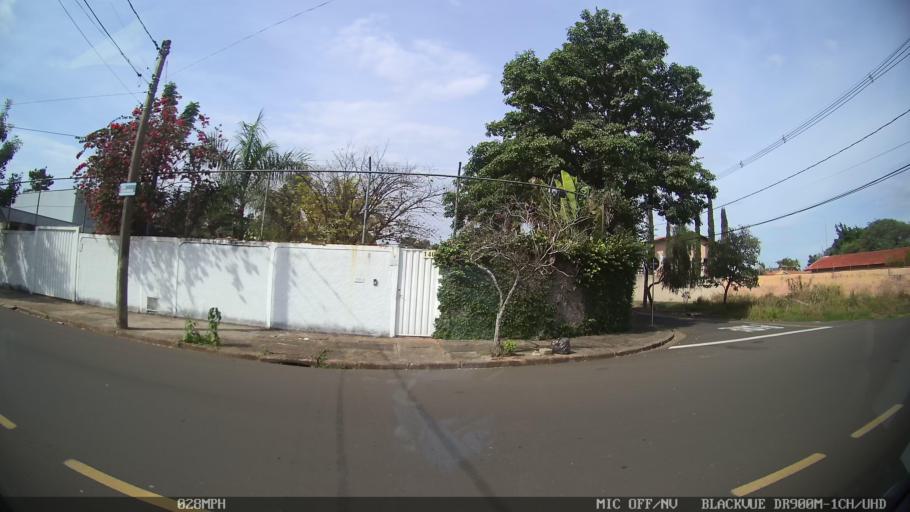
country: BR
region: Sao Paulo
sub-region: Piracicaba
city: Piracicaba
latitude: -22.7108
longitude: -47.6729
